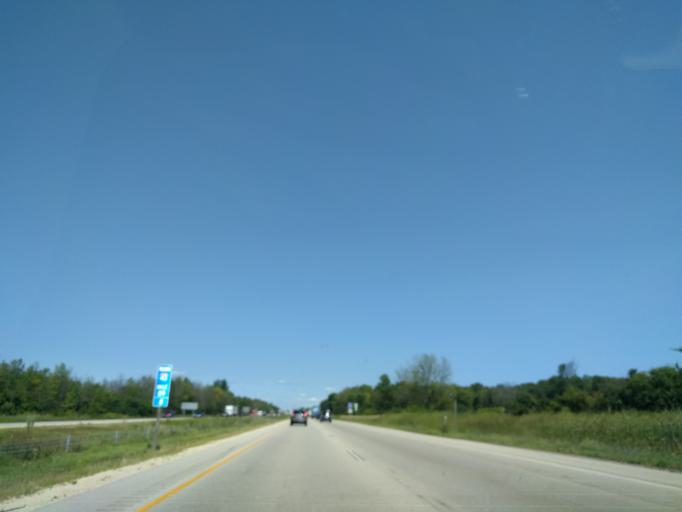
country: US
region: Wisconsin
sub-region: Ozaukee County
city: Grafton
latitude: 43.2844
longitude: -87.9212
